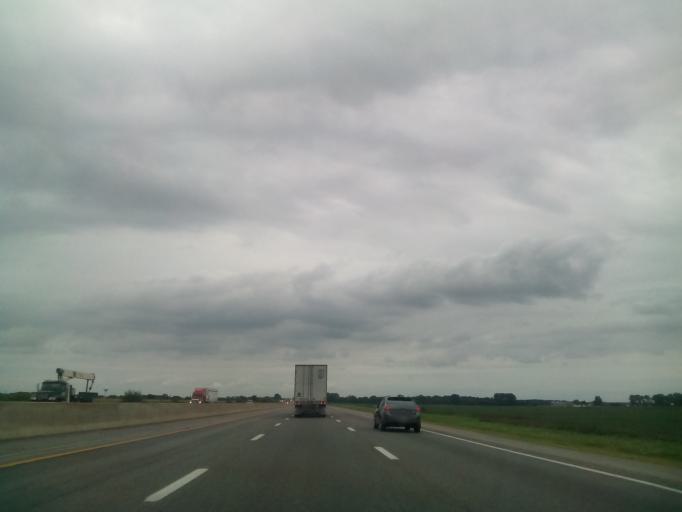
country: US
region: Ohio
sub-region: Erie County
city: Milan
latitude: 41.3306
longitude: -82.6584
